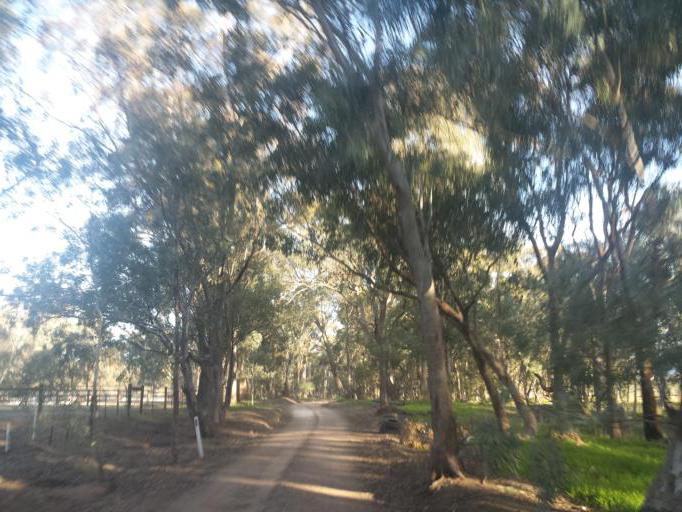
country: AU
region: Victoria
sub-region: Murrindindi
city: Kinglake West
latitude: -37.0272
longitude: 145.2323
